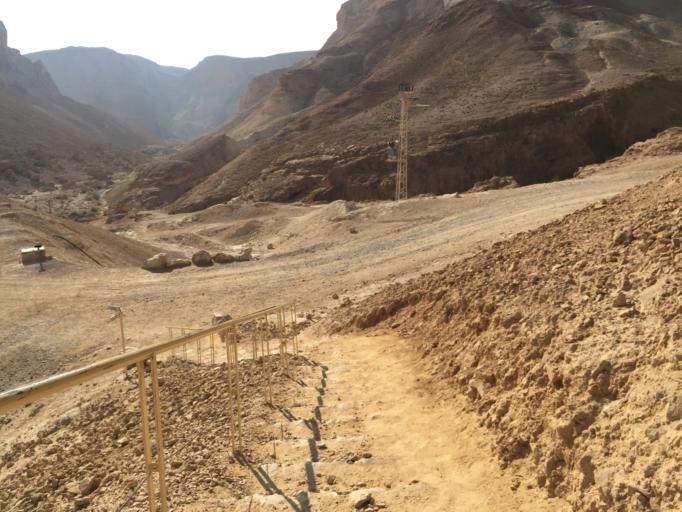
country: IL
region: Southern District
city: `En Boqeq
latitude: 31.3173
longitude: 35.3499
